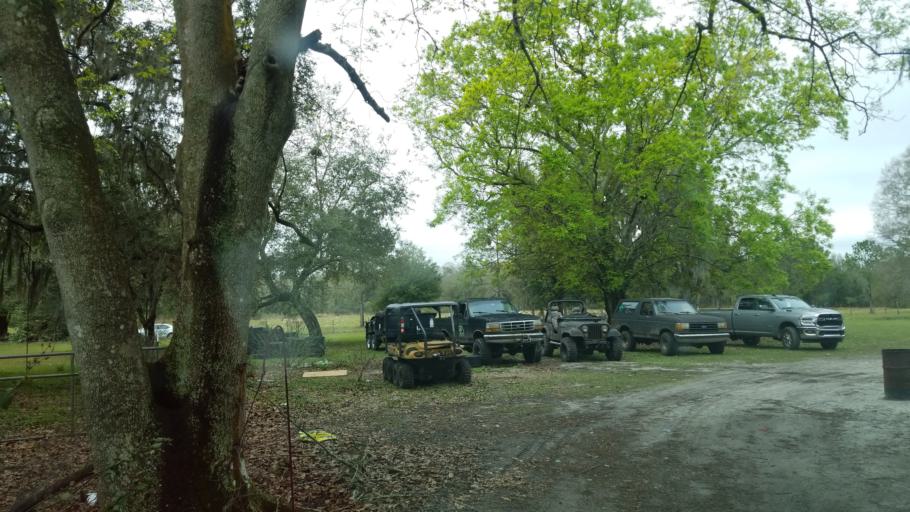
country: US
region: Florida
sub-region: Lake County
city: Groveland
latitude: 28.3841
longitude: -81.8542
